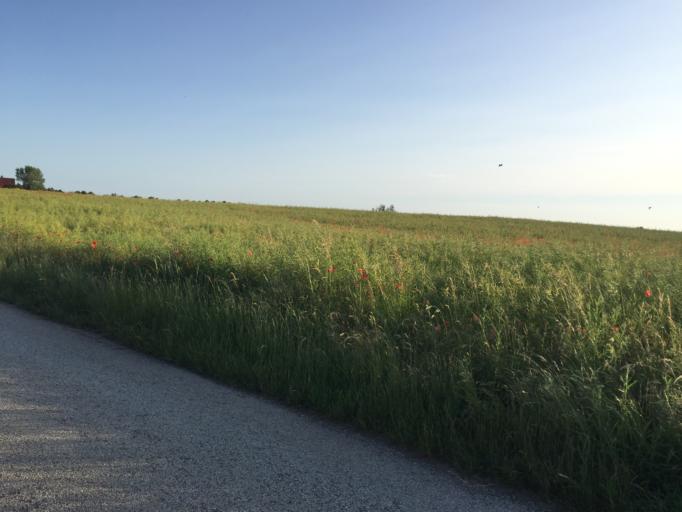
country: DK
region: Zealand
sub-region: Slagelse Kommune
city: Skaelskor
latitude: 55.2206
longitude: 11.1857
